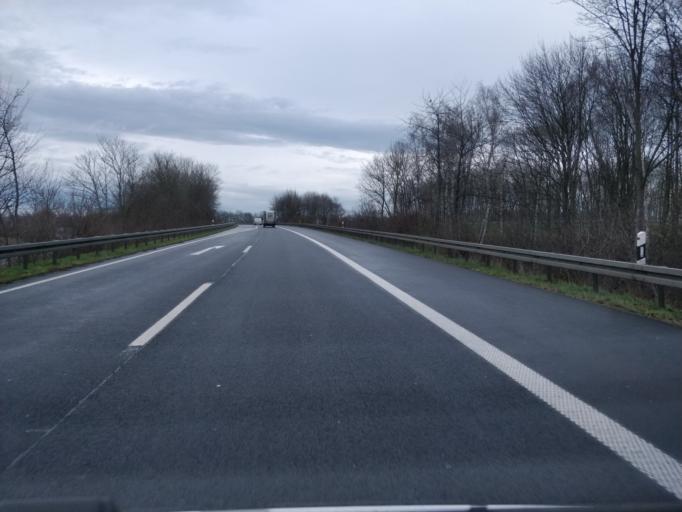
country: DE
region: North Rhine-Westphalia
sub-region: Regierungsbezirk Koln
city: Weilerswist
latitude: 50.7687
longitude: 6.8225
